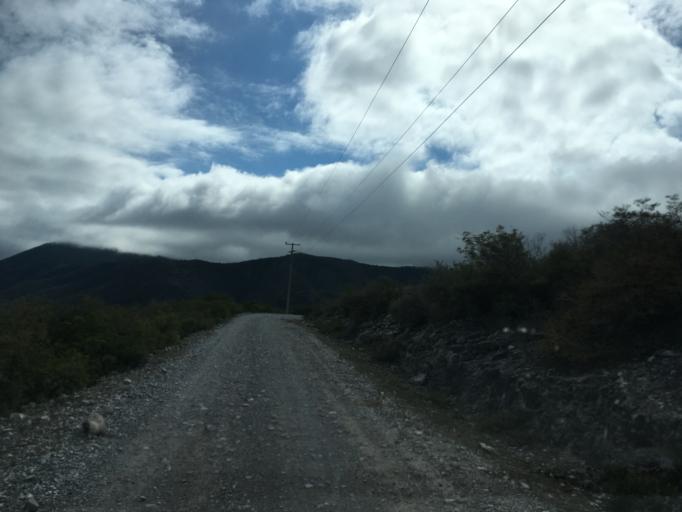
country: MX
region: Hidalgo
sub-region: Metztitlan
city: Fontezuelas
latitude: 20.6369
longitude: -98.8531
